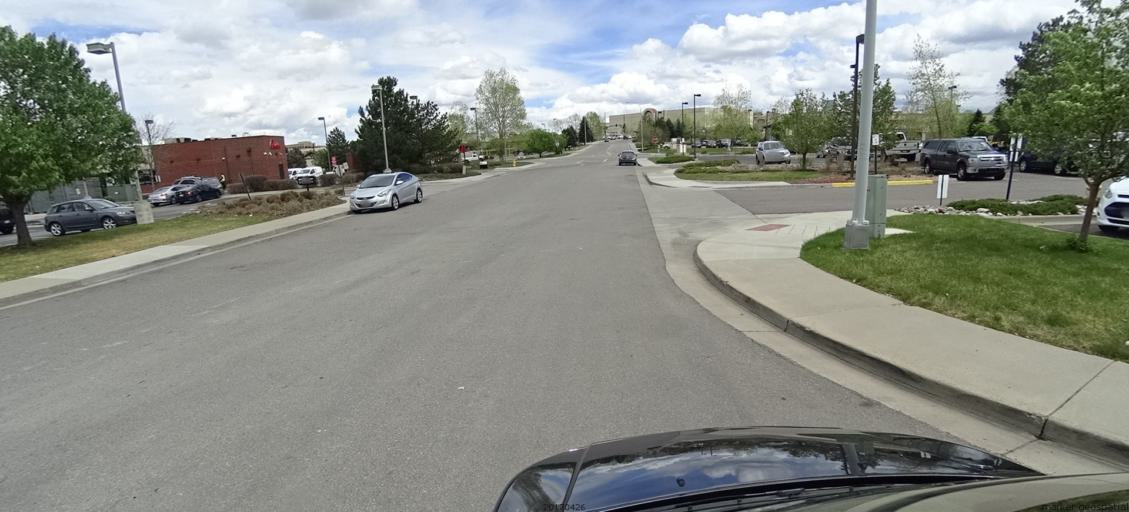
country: US
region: Colorado
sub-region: Adams County
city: Lone Tree
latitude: 39.5649
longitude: -104.8842
